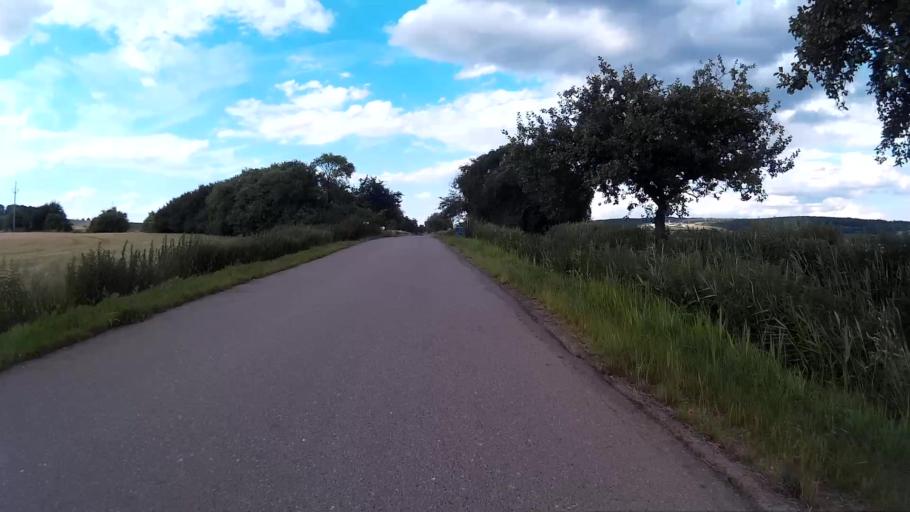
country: CZ
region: South Moravian
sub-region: Okres Brno-Venkov
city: Rosice
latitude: 49.1960
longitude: 16.3979
